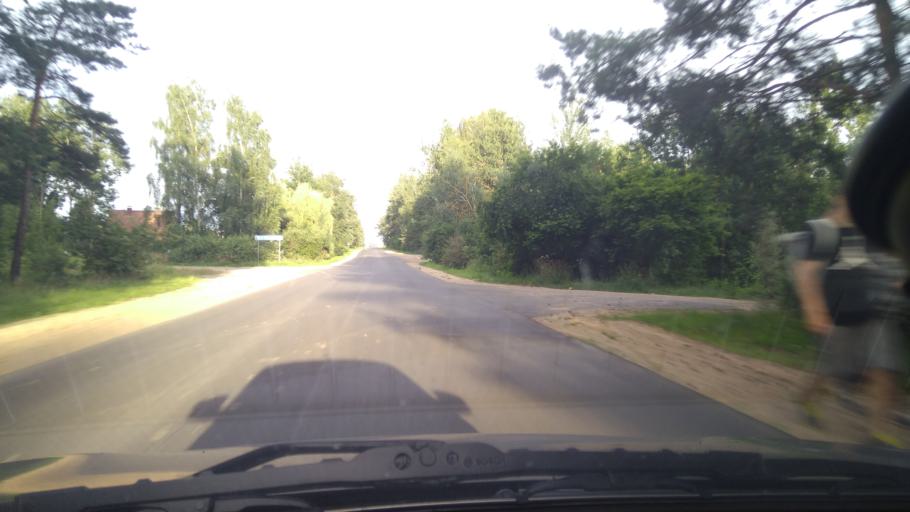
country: BY
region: Minsk
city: Rudzyensk
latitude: 53.6127
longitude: 27.7926
